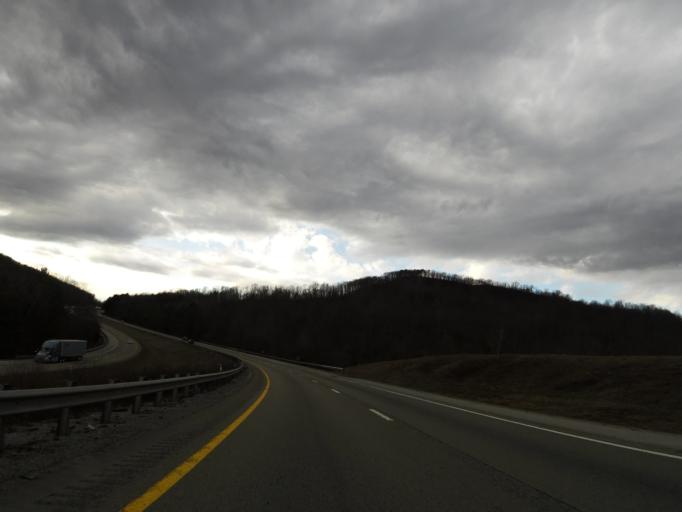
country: US
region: Tennessee
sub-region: Cumberland County
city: Fairfield Glade
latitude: 35.8969
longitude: -84.8434
